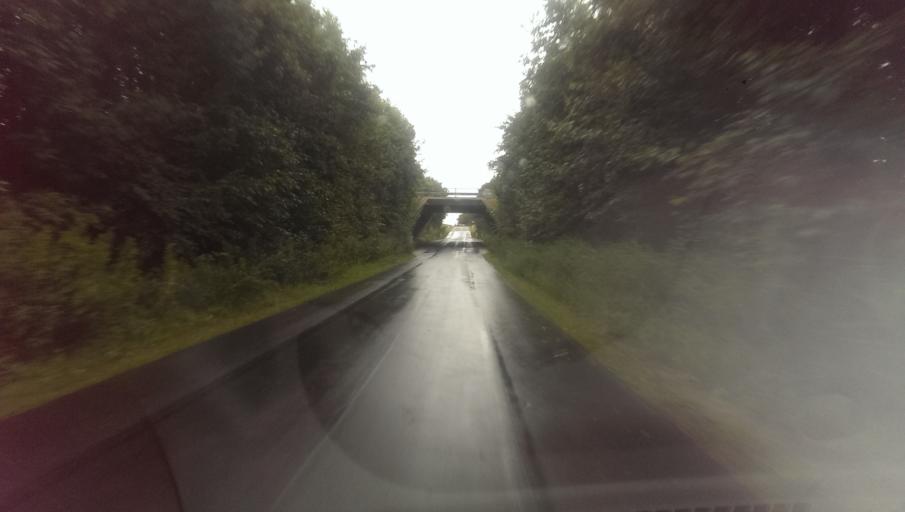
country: DK
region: South Denmark
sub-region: Esbjerg Kommune
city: Tjaereborg
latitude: 55.5166
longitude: 8.5253
